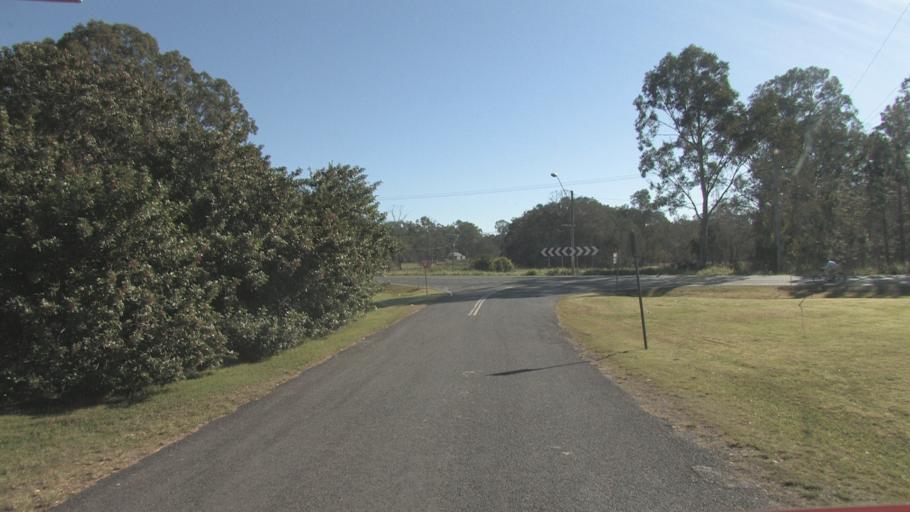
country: AU
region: Queensland
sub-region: Gold Coast
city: Yatala
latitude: -27.6851
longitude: 153.2600
